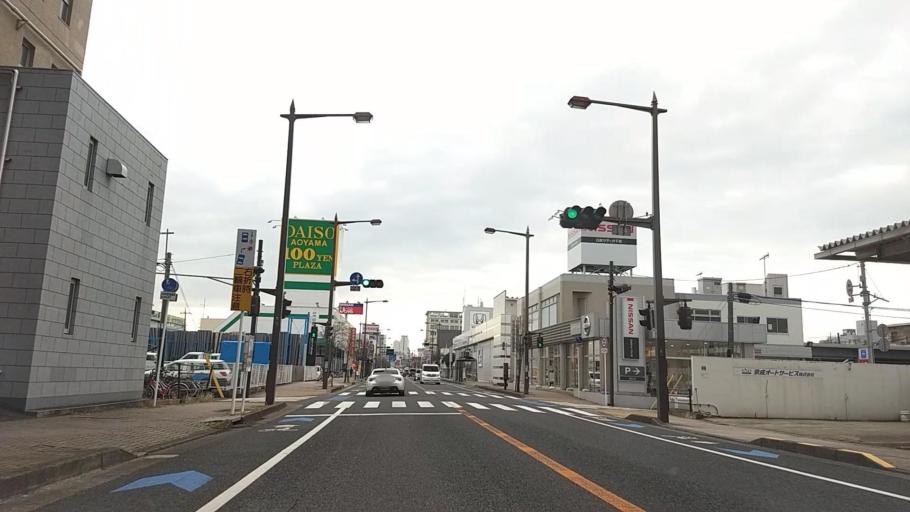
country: JP
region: Chiba
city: Chiba
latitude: 35.6099
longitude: 140.1407
